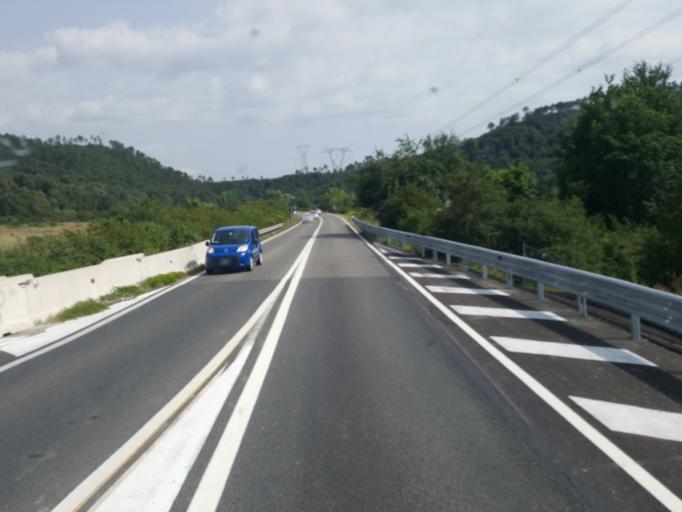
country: IT
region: Tuscany
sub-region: Provincia di Grosseto
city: Civitella Marittima
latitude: 43.0243
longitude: 11.2802
